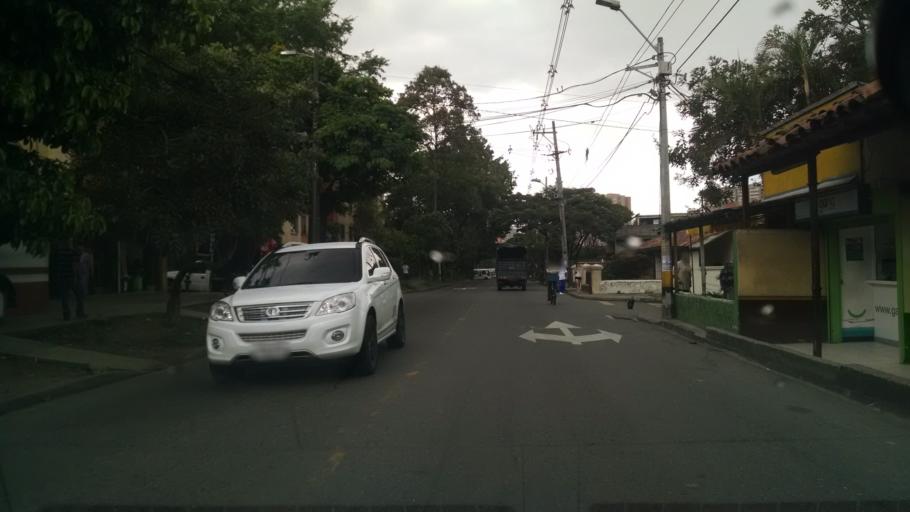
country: CO
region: Antioquia
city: Medellin
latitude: 6.2682
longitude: -75.5871
